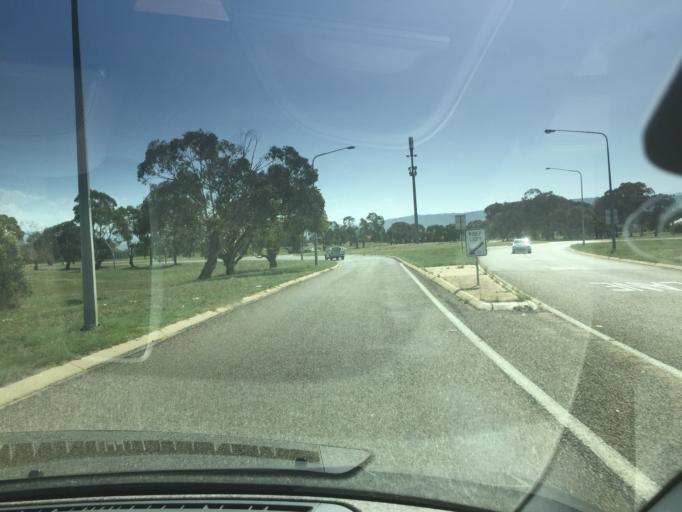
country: AU
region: Australian Capital Territory
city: Macarthur
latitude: -35.4232
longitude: 149.0911
